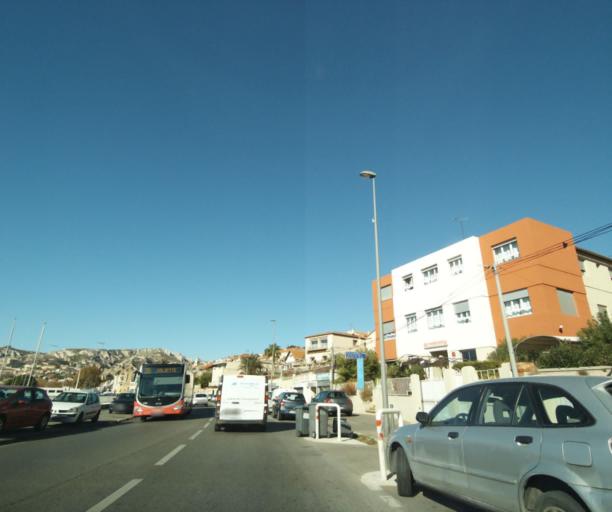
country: FR
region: Provence-Alpes-Cote d'Azur
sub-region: Departement des Bouches-du-Rhone
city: Marseille 16
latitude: 43.3587
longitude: 5.3185
